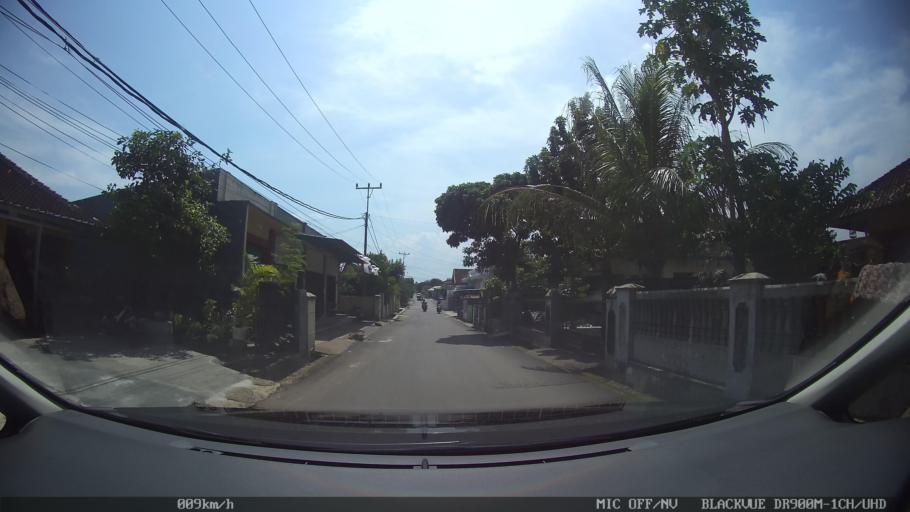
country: ID
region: Lampung
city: Kedaton
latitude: -5.3608
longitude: 105.2530
